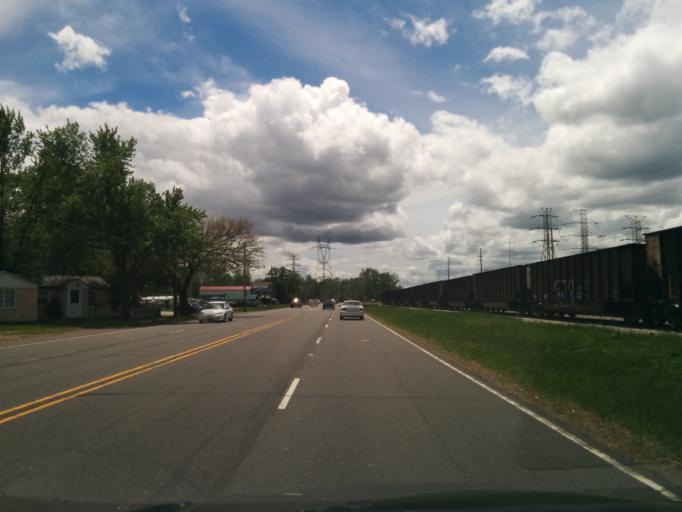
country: US
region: Indiana
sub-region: LaPorte County
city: Michigan City
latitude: 41.7089
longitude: -86.9215
